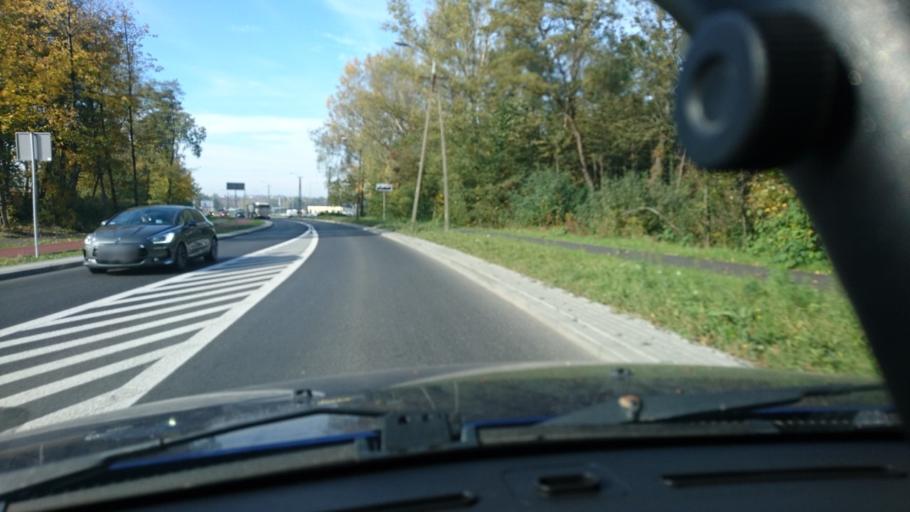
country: PL
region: Silesian Voivodeship
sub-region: Powiat bielski
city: Mazancowice
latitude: 49.8240
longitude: 18.9750
